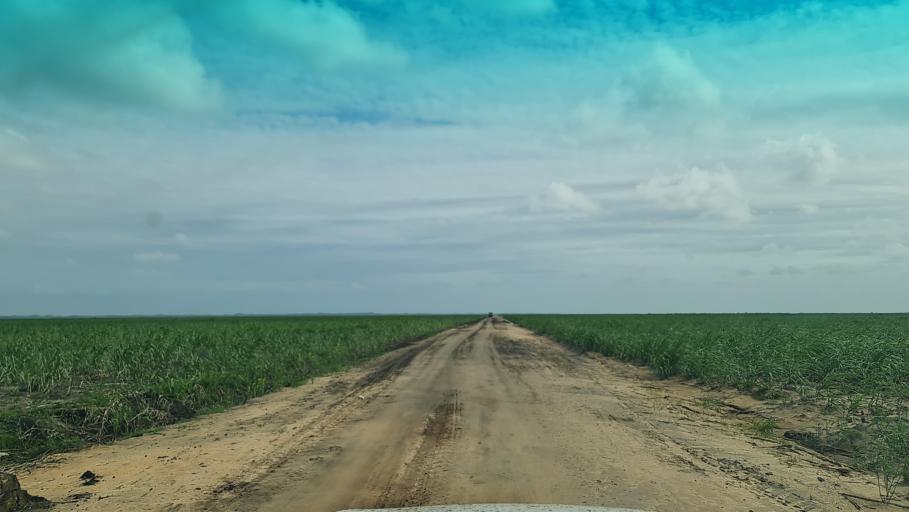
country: MZ
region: Maputo
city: Manhica
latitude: -25.4733
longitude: 32.8170
